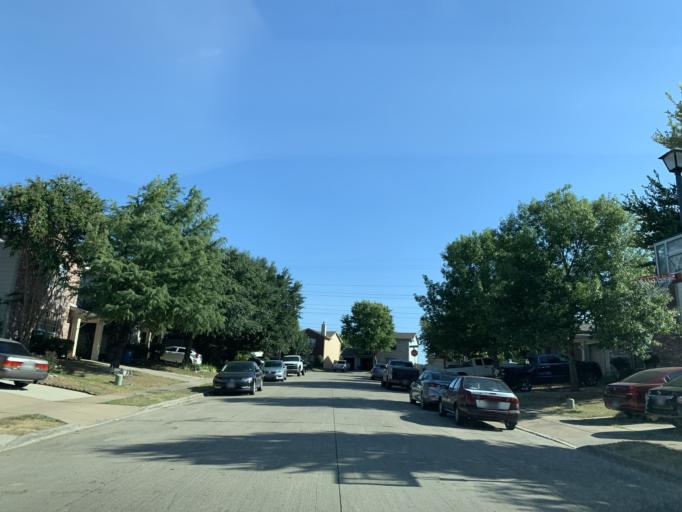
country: US
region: Texas
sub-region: Dallas County
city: Cockrell Hill
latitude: 32.7075
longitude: -96.8970
